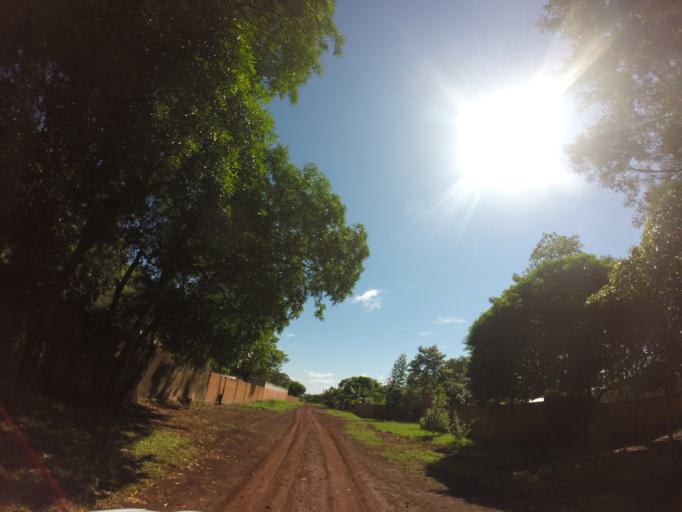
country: PY
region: Alto Parana
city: Ciudad del Este
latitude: -25.4213
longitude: -54.6476
